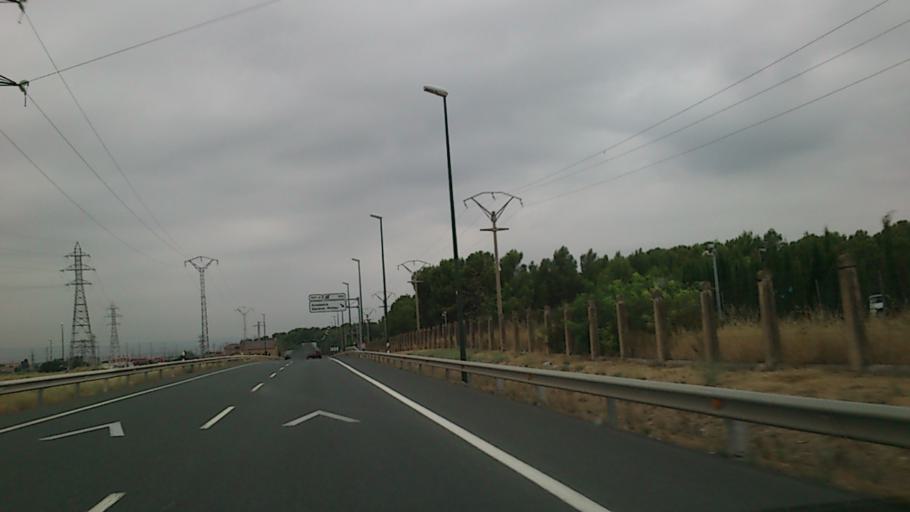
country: ES
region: Aragon
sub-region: Provincia de Zaragoza
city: Zaragoza
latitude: 41.7047
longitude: -0.8655
